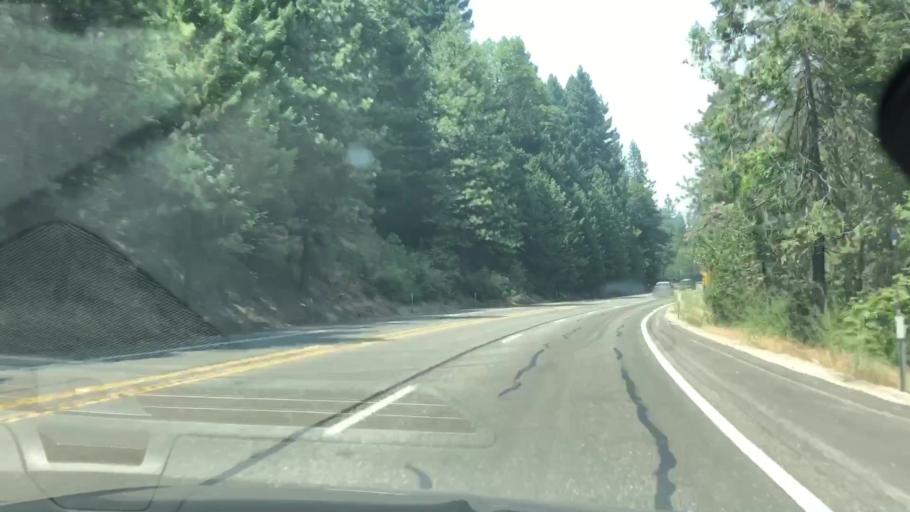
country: US
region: California
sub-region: El Dorado County
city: Pollock Pines
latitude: 38.7649
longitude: -120.5506
